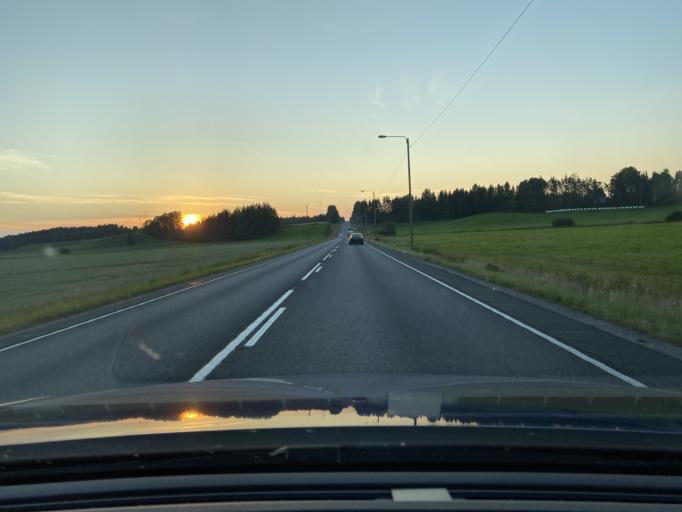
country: FI
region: Pirkanmaa
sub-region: Luoteis-Pirkanmaa
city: Ikaalinen
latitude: 61.7670
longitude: 23.0177
